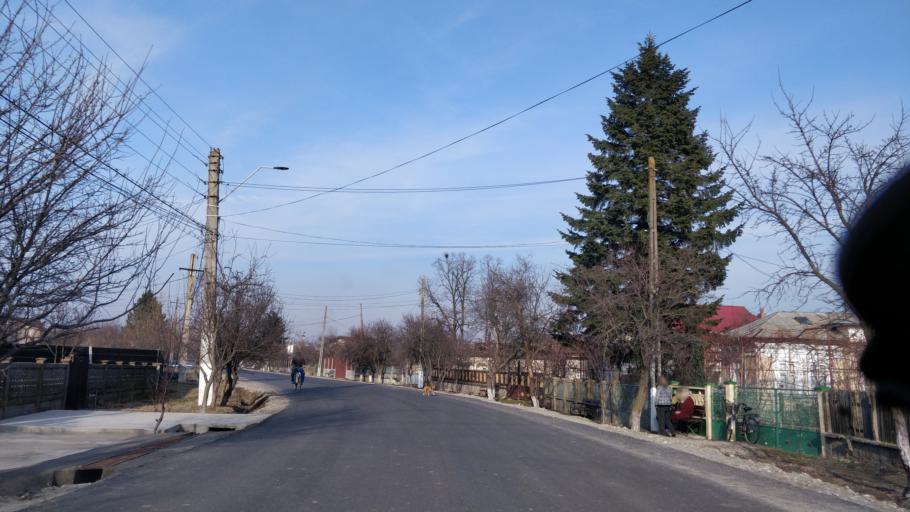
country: RO
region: Giurgiu
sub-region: Comuna Ulmi
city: Trestieni
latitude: 44.5089
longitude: 25.7631
